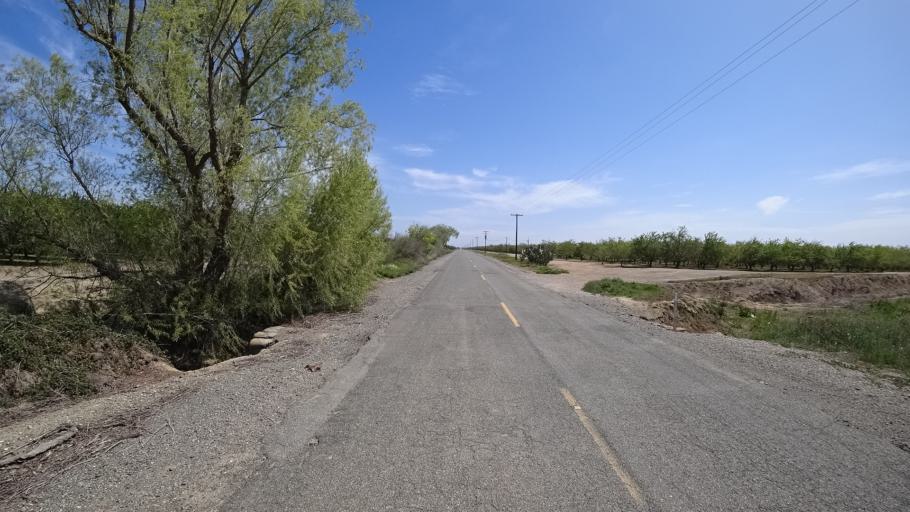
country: US
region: California
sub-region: Glenn County
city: Hamilton City
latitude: 39.6525
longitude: -122.0964
